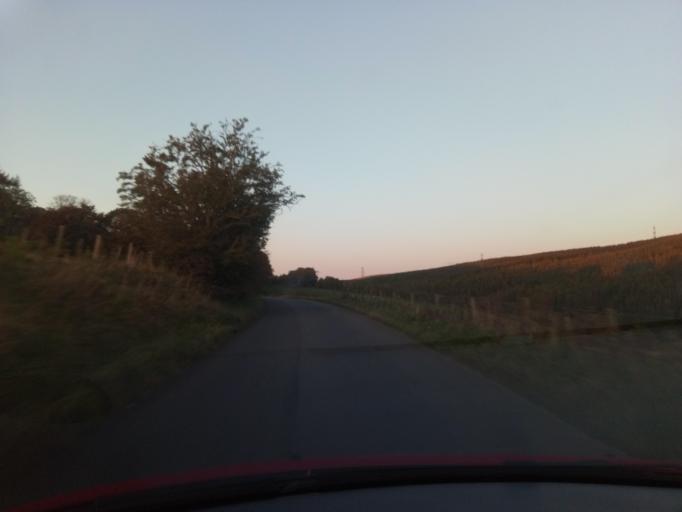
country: GB
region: Scotland
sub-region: Fife
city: Pathhead
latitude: 55.7886
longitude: -2.8944
